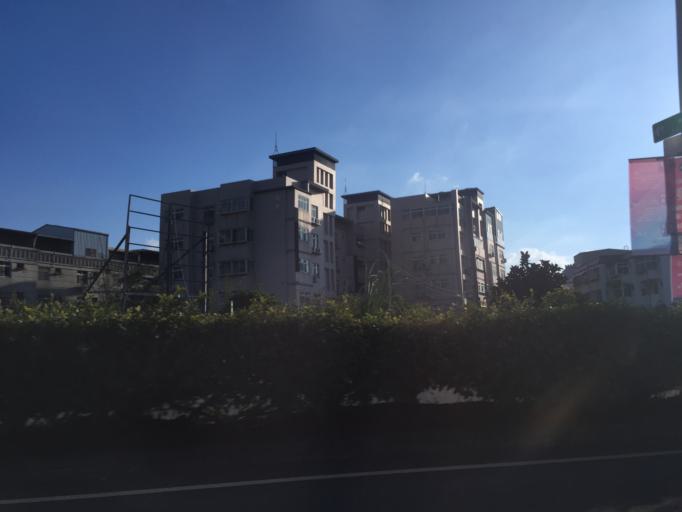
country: TW
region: Taiwan
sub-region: Hsinchu
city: Hsinchu
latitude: 24.6943
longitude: 120.8948
